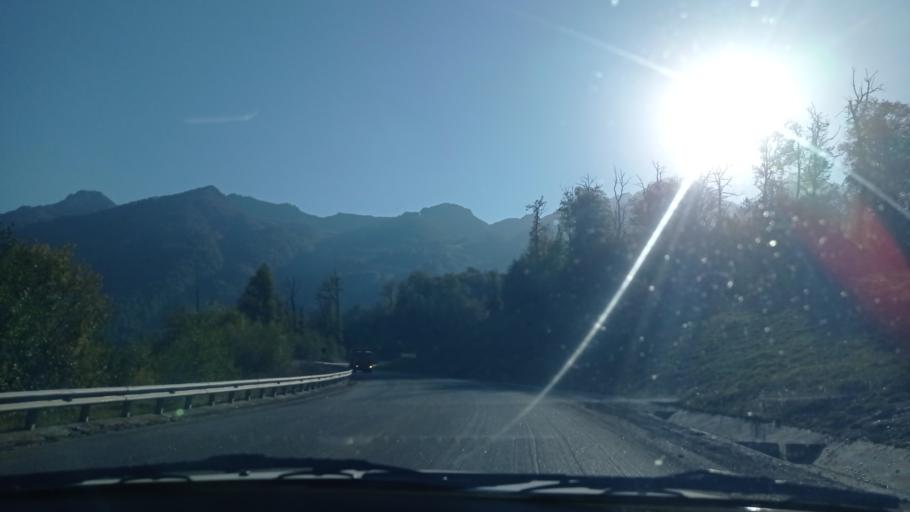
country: RU
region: Krasnodarskiy
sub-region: Sochi City
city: Krasnaya Polyana
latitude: 43.6688
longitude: 40.3008
